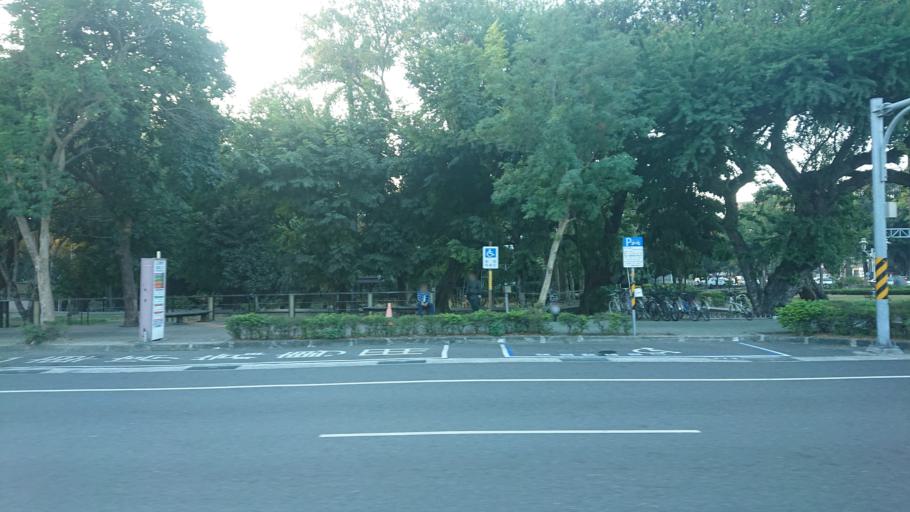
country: TW
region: Taiwan
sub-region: Tainan
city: Tainan
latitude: 23.0036
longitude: 120.2134
